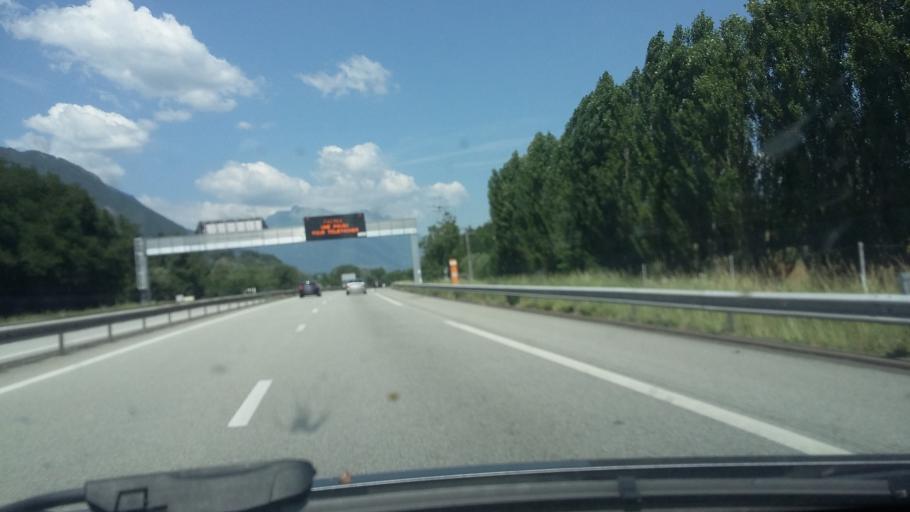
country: FR
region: Rhone-Alpes
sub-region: Departement de la Savoie
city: Montmelian
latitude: 45.4874
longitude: 6.0445
